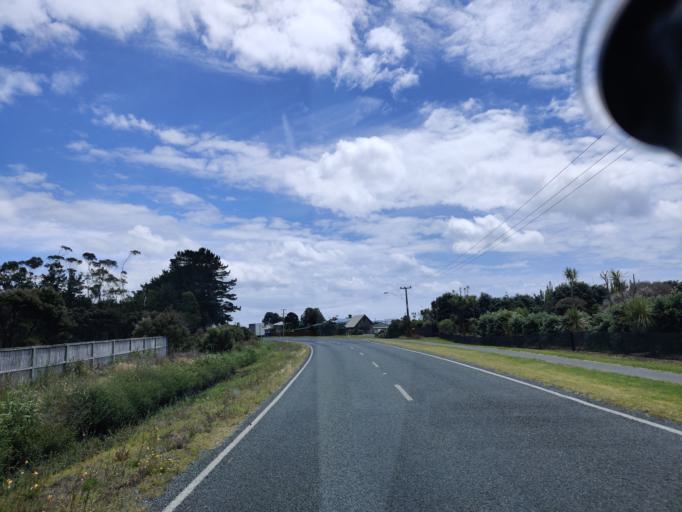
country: NZ
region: Northland
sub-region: Far North District
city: Kaitaia
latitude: -34.8247
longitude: 173.1277
